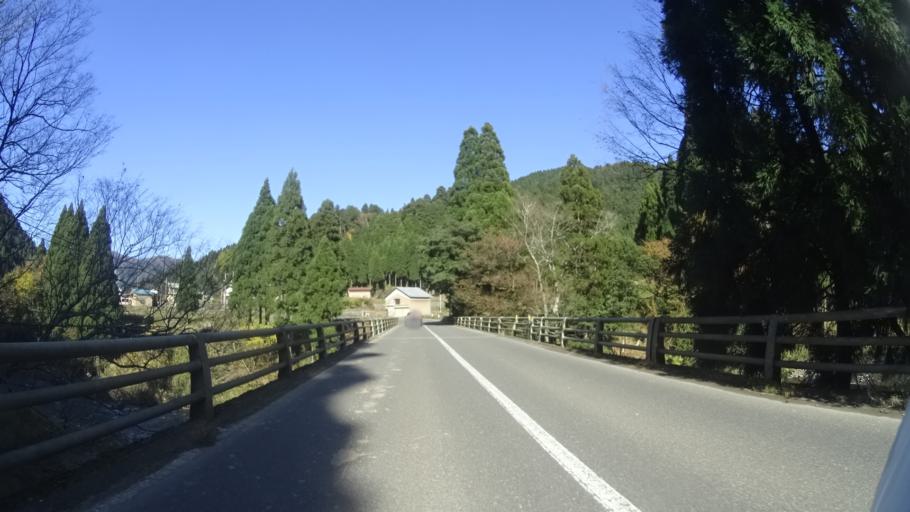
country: JP
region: Fukui
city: Ono
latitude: 35.9336
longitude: 136.3633
